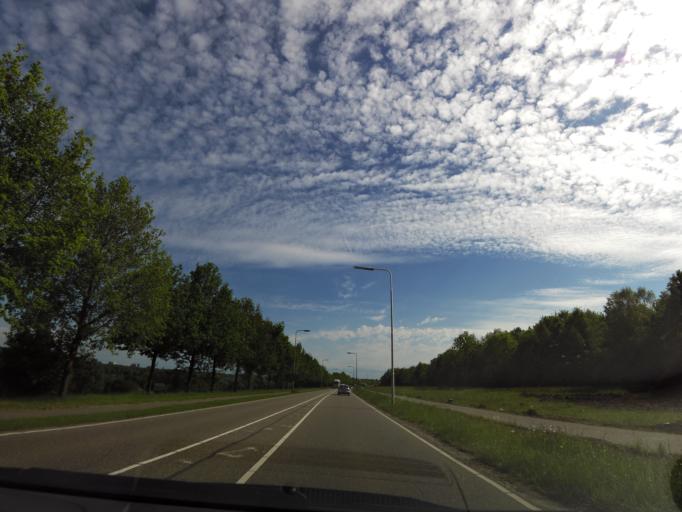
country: NL
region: Limburg
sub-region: Gemeente Kerkrade
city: Kerkrade
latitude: 50.8833
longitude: 6.0433
